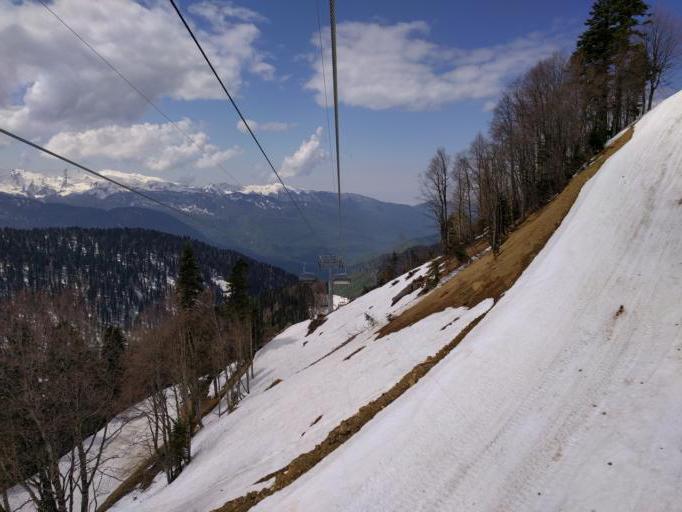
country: RU
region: Krasnodarskiy
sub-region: Sochi City
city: Krasnaya Polyana
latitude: 43.6193
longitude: 40.3041
